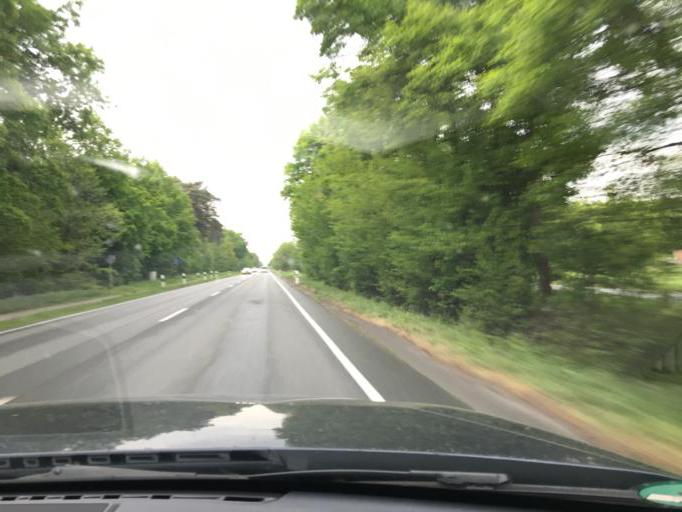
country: DE
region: North Rhine-Westphalia
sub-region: Regierungsbezirk Munster
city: Greven
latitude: 52.1368
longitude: 7.5706
